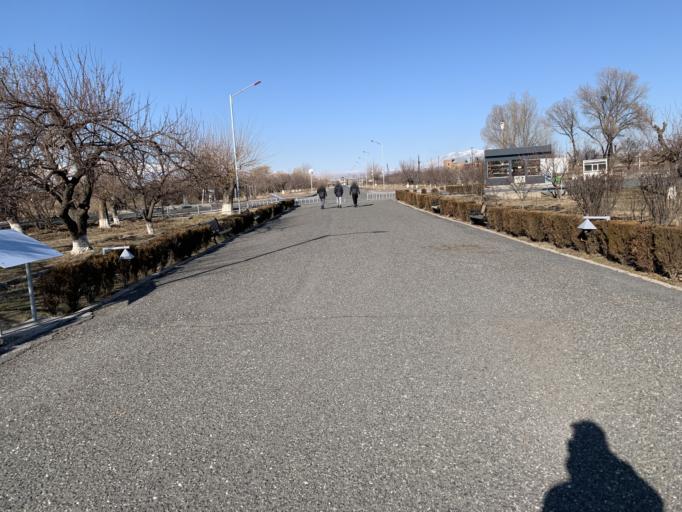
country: AM
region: Armavir
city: Voskehat
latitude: 40.1610
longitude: 44.3367
